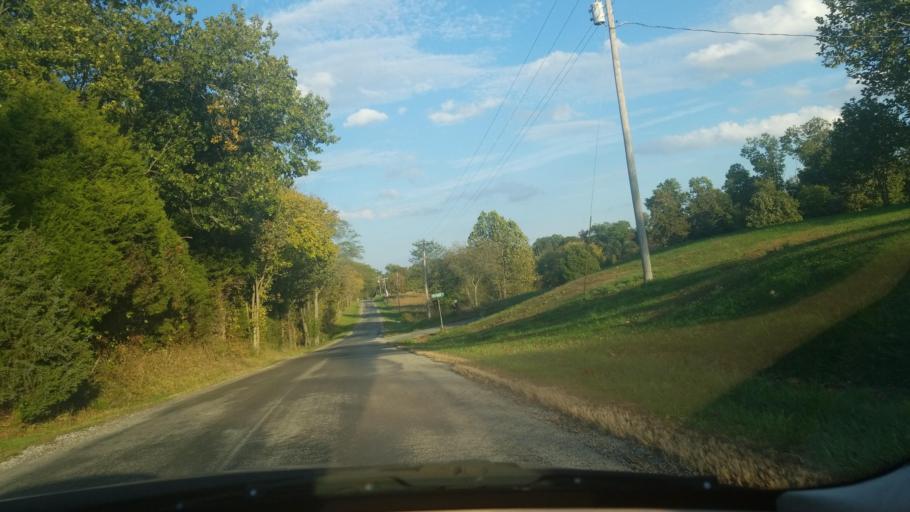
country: US
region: Illinois
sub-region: Saline County
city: Carrier Mills
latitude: 37.7706
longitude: -88.7675
